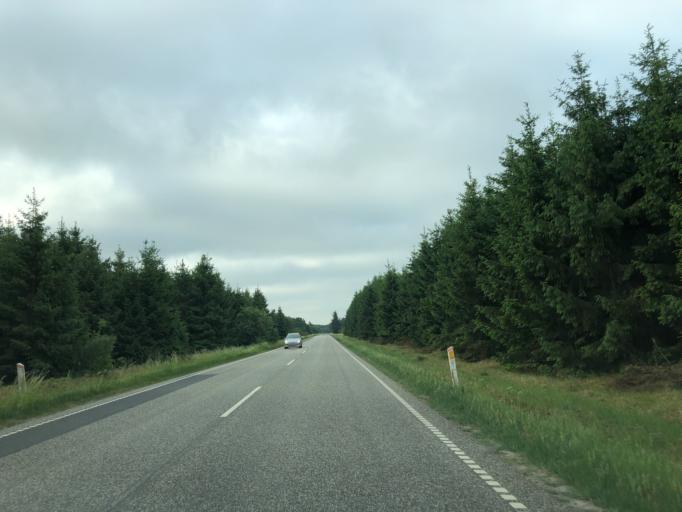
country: DK
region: South Denmark
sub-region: Vejle Kommune
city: Give
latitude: 55.8930
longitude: 9.2110
